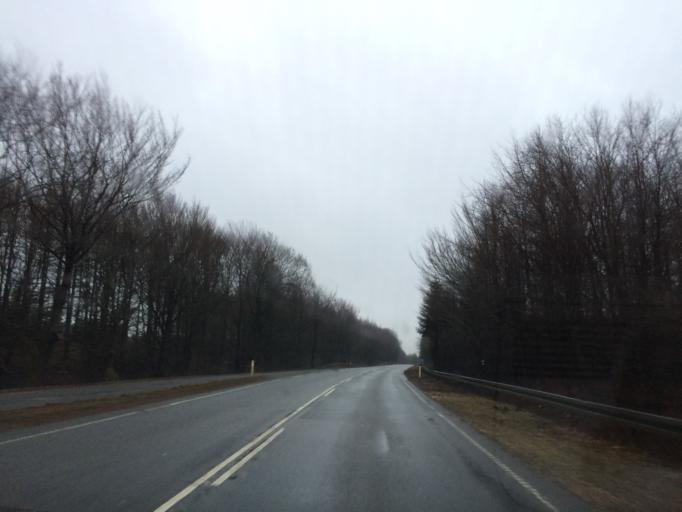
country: DK
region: North Denmark
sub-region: Mariagerfjord Kommune
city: Arden
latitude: 56.7930
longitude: 9.8214
